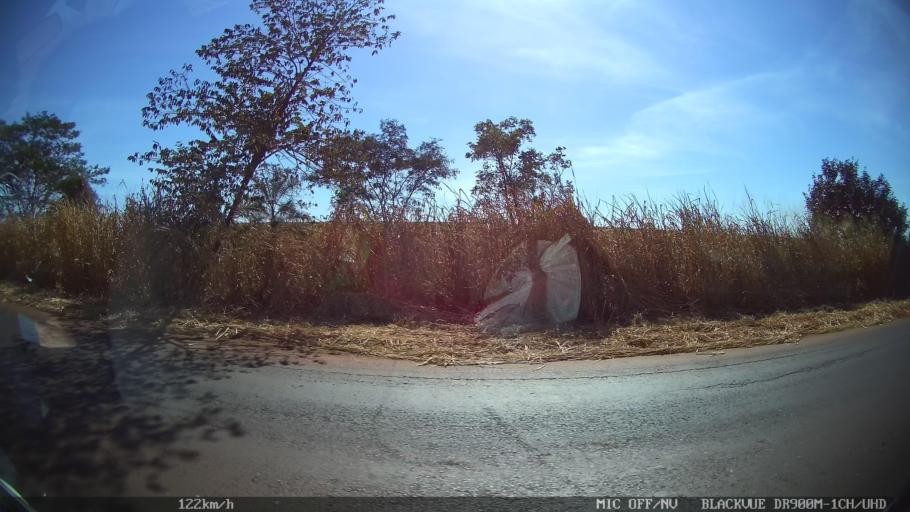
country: BR
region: Sao Paulo
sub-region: Barretos
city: Barretos
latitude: -20.4614
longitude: -48.4680
